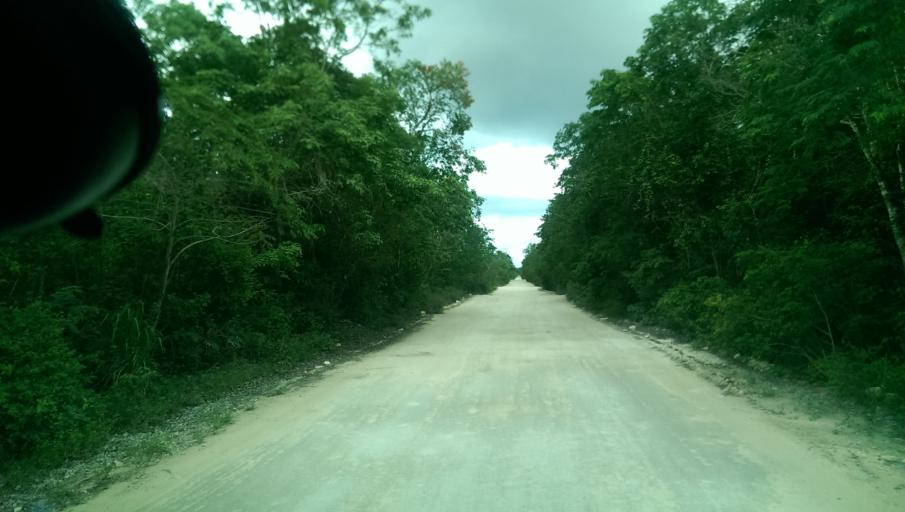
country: MX
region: Quintana Roo
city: Playa del Carmen
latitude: 20.5924
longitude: -87.1442
